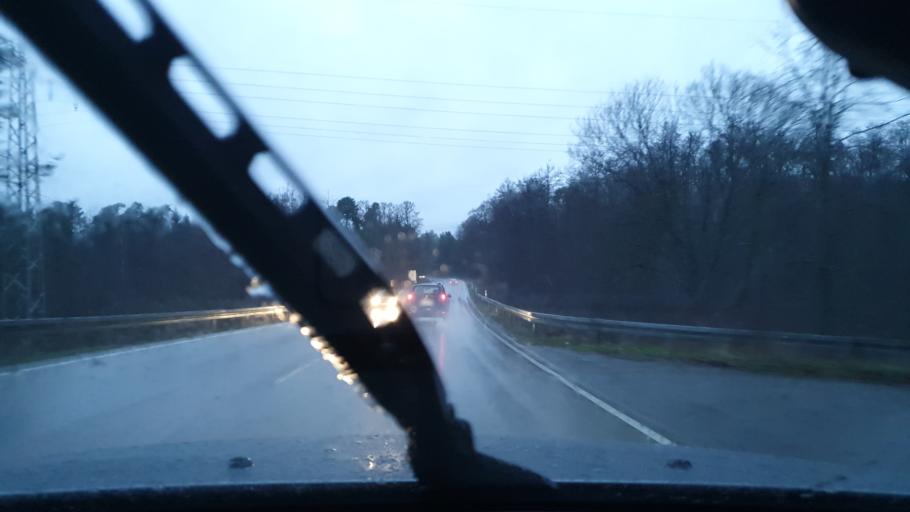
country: DE
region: Rheinland-Pfalz
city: Bechhofen
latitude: 49.3642
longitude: 7.3807
